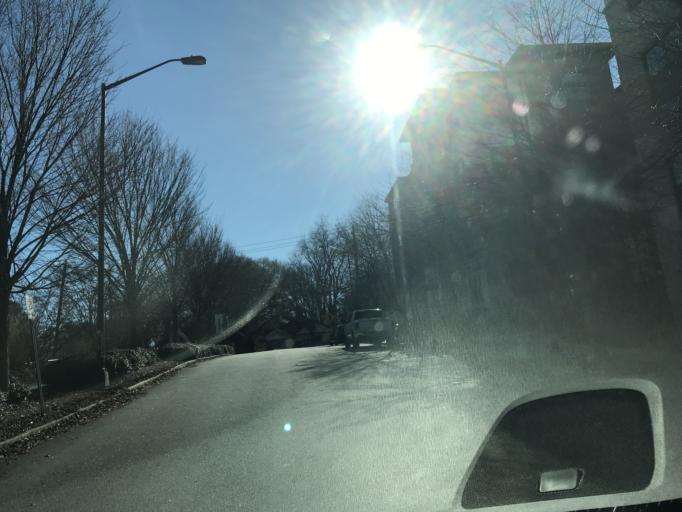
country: US
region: Georgia
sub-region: Fulton County
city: Atlanta
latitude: 33.7656
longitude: -84.3652
